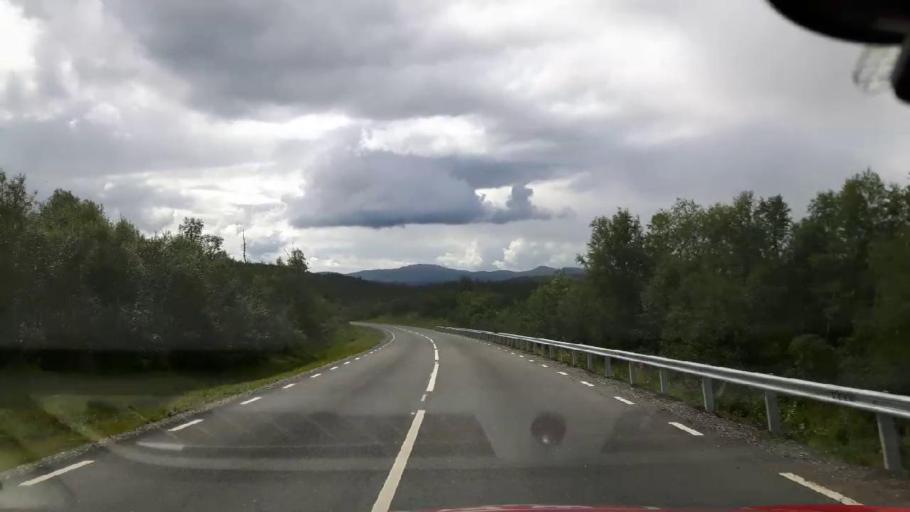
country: NO
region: Nordland
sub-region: Hattfjelldal
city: Hattfjelldal
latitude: 64.9854
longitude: 14.2131
